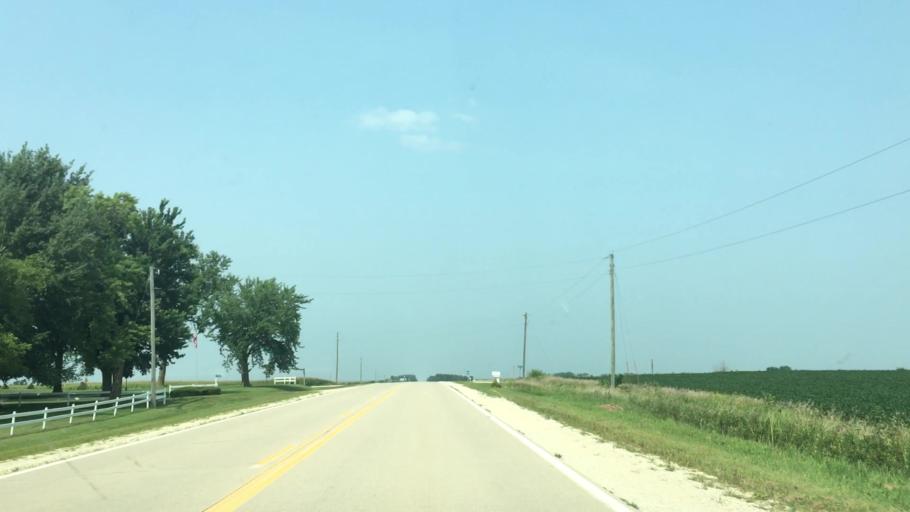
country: US
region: Iowa
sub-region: Fayette County
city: Fayette
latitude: 42.7440
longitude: -91.8041
